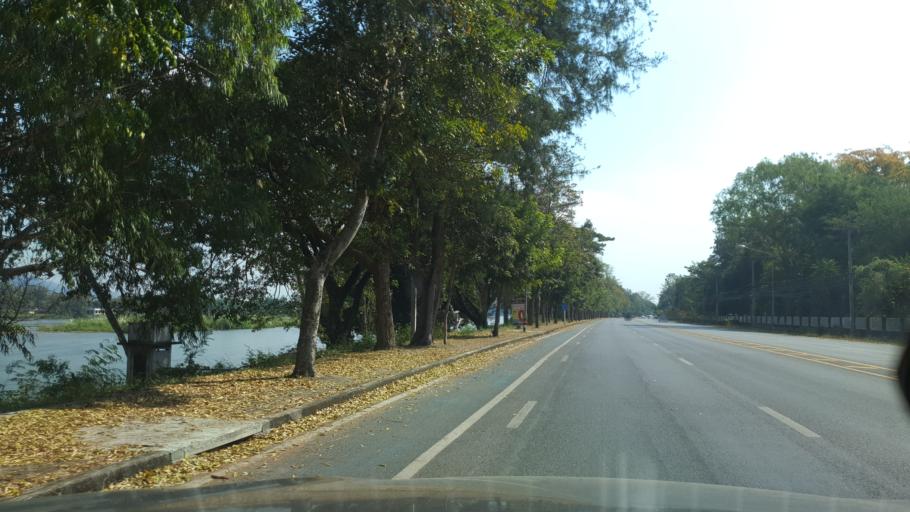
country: TH
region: Tak
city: Tak
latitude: 16.8741
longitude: 99.1175
